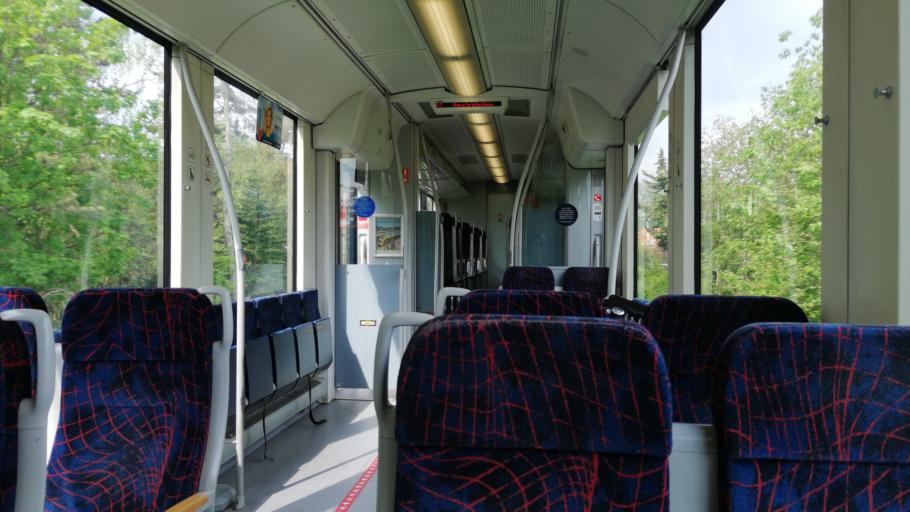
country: DK
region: Capital Region
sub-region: Helsingor Kommune
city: Hornbaek
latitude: 56.0971
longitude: 12.3926
